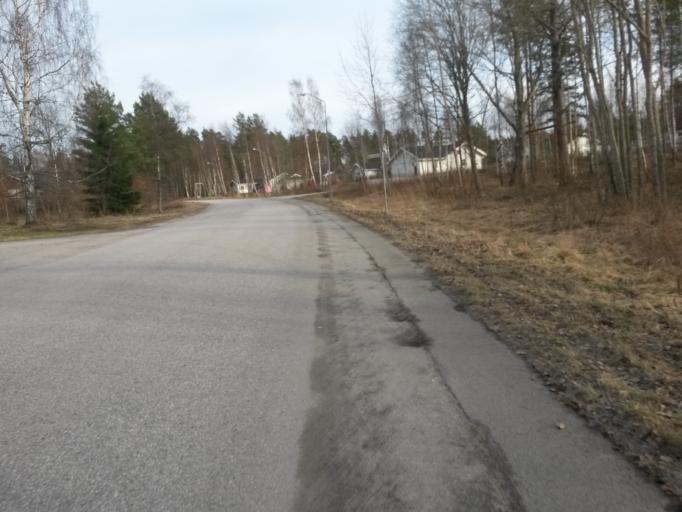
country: SE
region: Vaestra Goetaland
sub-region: Herrljunga Kommun
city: Herrljunga
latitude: 58.0683
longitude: 13.0278
